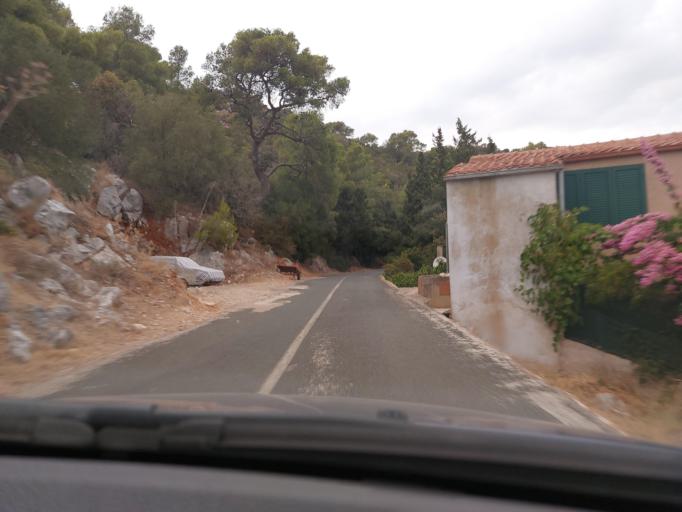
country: HR
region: Dubrovacko-Neretvanska
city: Smokvica
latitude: 42.7672
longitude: 16.8932
